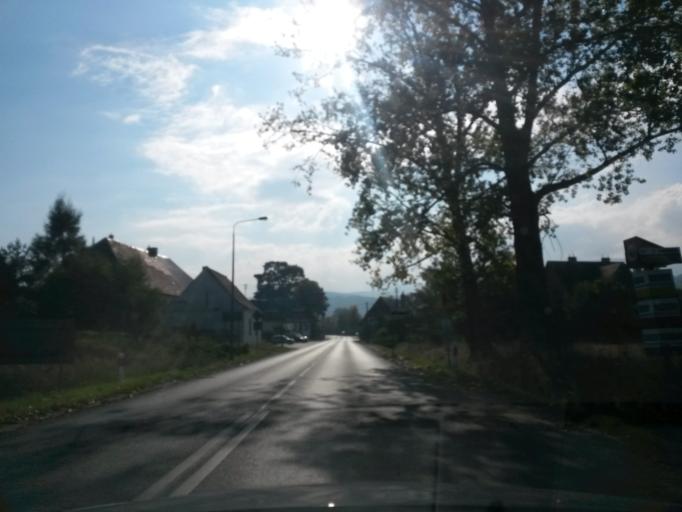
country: PL
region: Lower Silesian Voivodeship
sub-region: Powiat jeleniogorski
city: Podgorzyn
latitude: 50.8386
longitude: 15.6785
